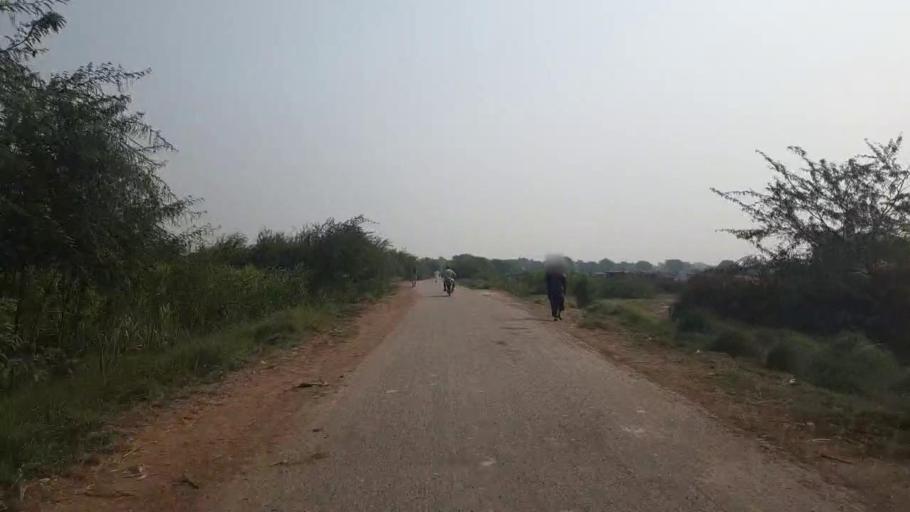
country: PK
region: Sindh
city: Tando Muhammad Khan
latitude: 25.2445
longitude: 68.5677
